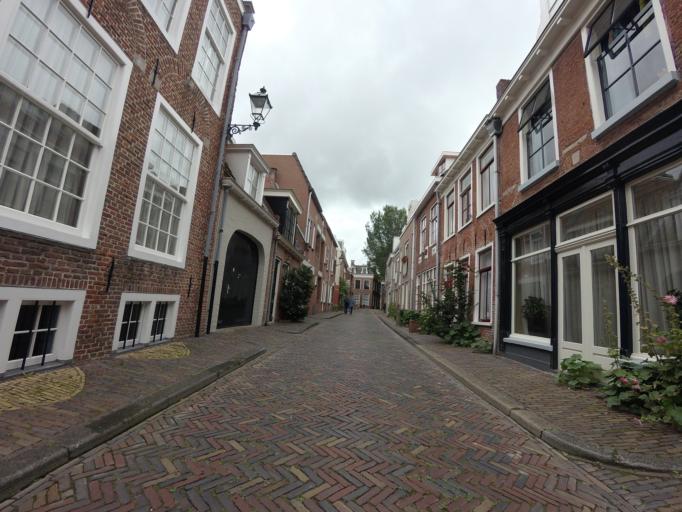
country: NL
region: Friesland
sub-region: Gemeente Leeuwarden
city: Leeuwarden
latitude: 53.2048
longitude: 5.7985
